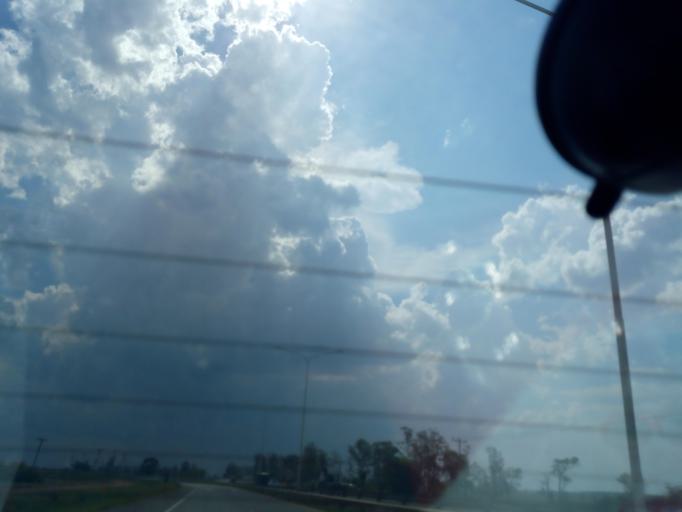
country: AR
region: Corrientes
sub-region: Departamento de Paso de los Libres
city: Paso de los Libres
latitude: -29.7220
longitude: -57.1680
